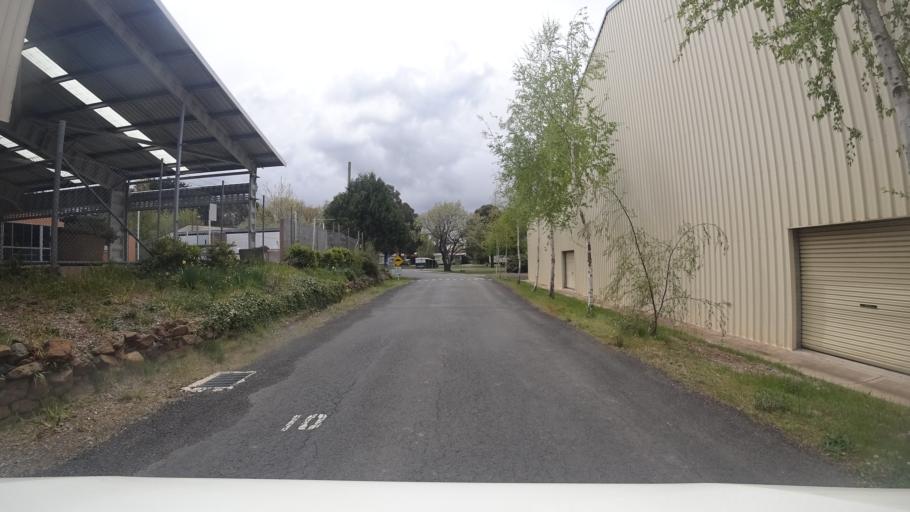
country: AU
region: New South Wales
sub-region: Oberon
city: Oberon
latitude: -33.7012
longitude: 149.8579
